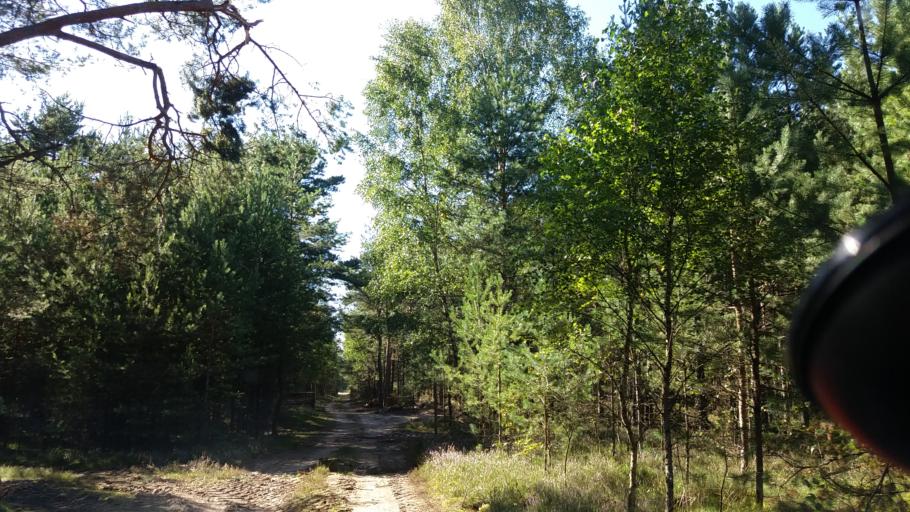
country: PL
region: West Pomeranian Voivodeship
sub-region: Powiat szczecinecki
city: Borne Sulinowo
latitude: 53.5743
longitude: 16.4932
